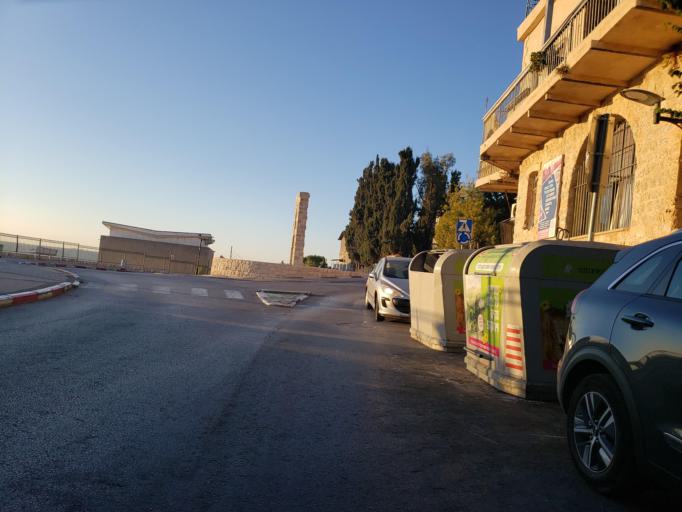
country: IL
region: Northern District
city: Safed
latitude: 32.9715
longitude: 35.4928
